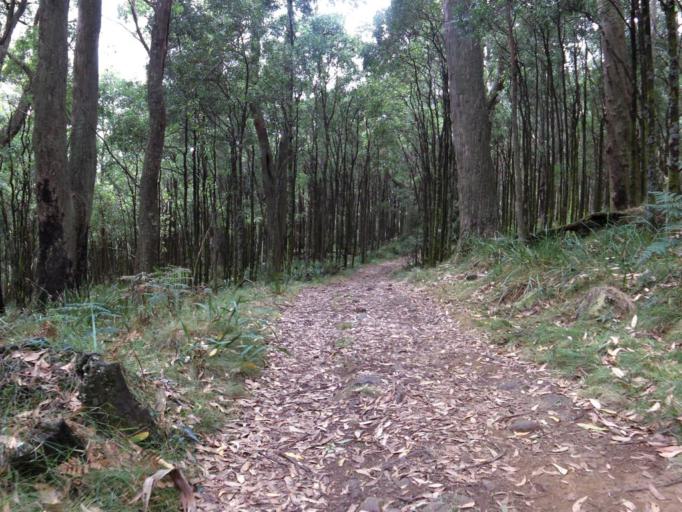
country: AU
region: Victoria
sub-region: Hume
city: Sunbury
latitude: -37.3731
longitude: 144.5763
